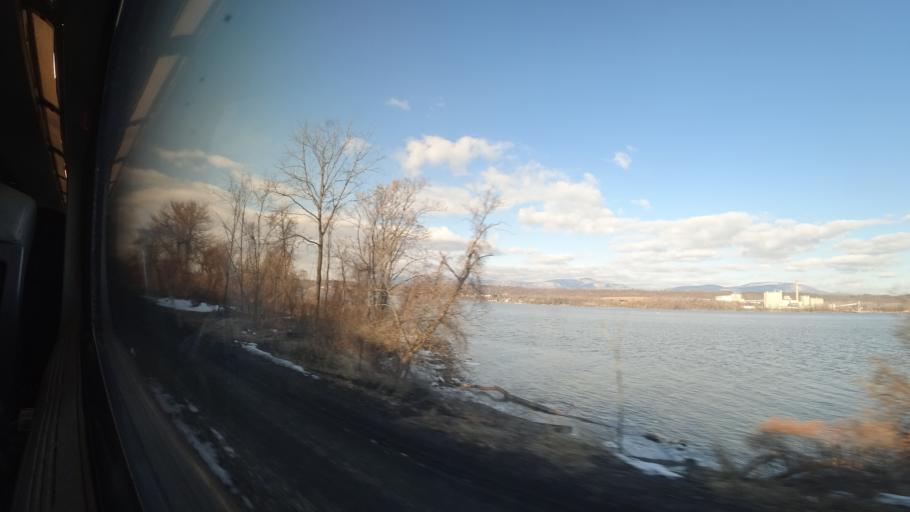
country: US
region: New York
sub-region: Dutchess County
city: Tivoli
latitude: 42.1321
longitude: -73.8994
